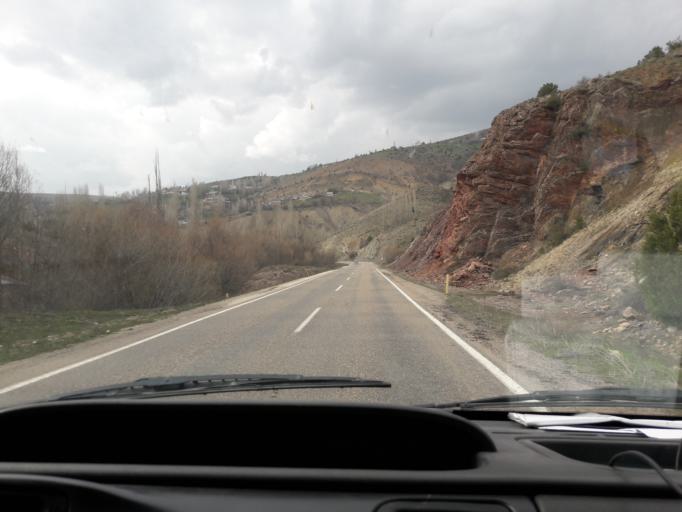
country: TR
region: Giresun
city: Alucra
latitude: 40.2683
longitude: 38.8842
